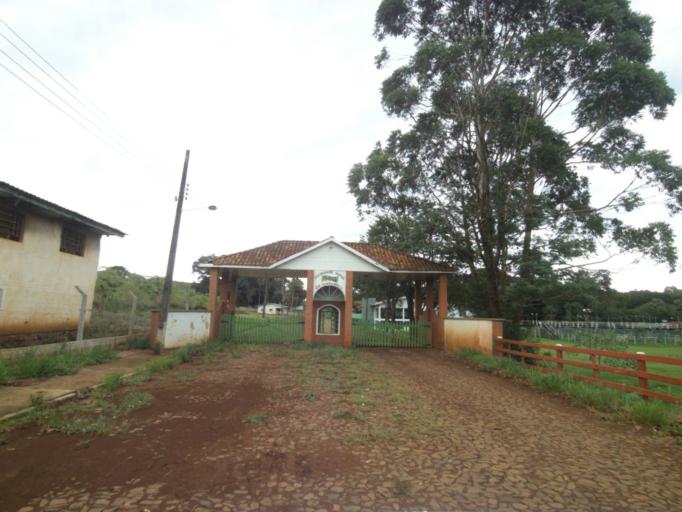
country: BR
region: Parana
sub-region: Guaraniacu
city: Guaraniacu
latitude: -25.1158
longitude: -52.8536
